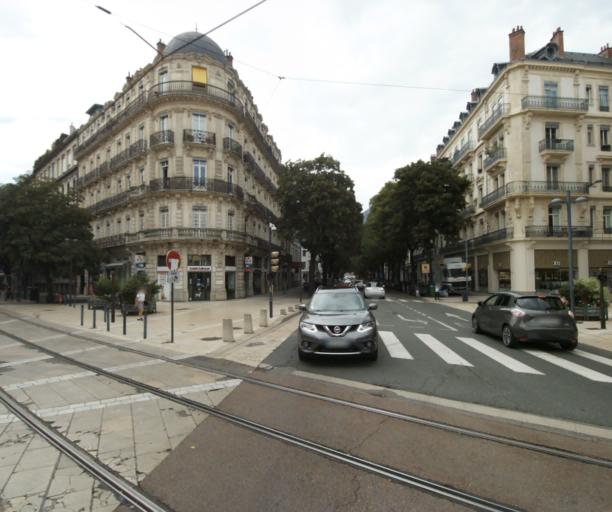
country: FR
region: Rhone-Alpes
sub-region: Departement de l'Isere
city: Saint-Martin-le-Vinoux
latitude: 45.1890
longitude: 5.7227
